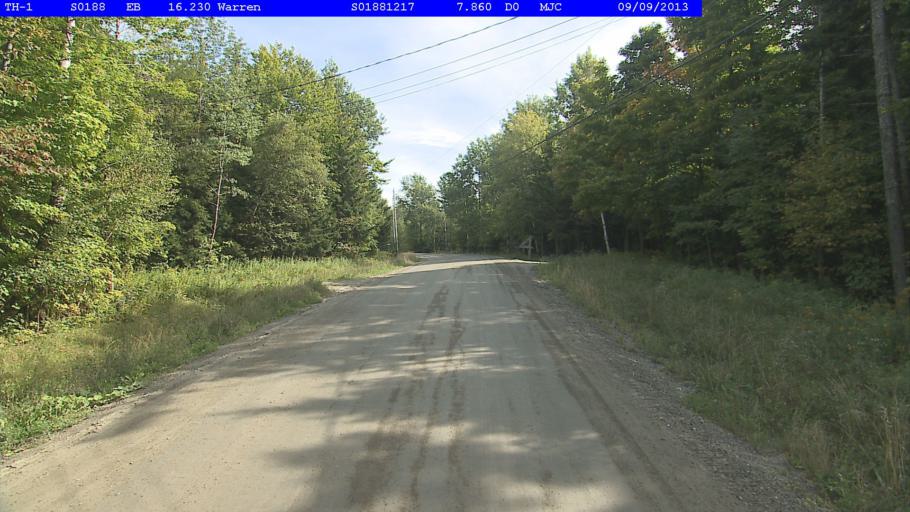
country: US
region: Vermont
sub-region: Washington County
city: Northfield
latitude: 44.1081
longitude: -72.7990
